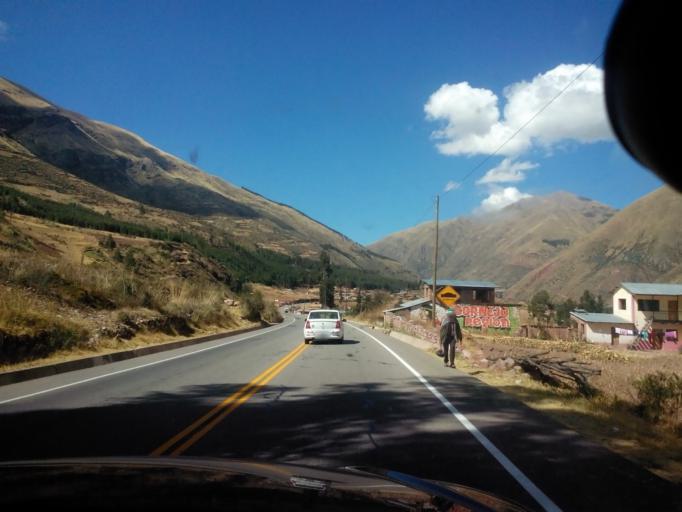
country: PE
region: Cusco
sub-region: Provincia de Quispicanchis
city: Cusipata
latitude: -13.9556
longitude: -71.4994
